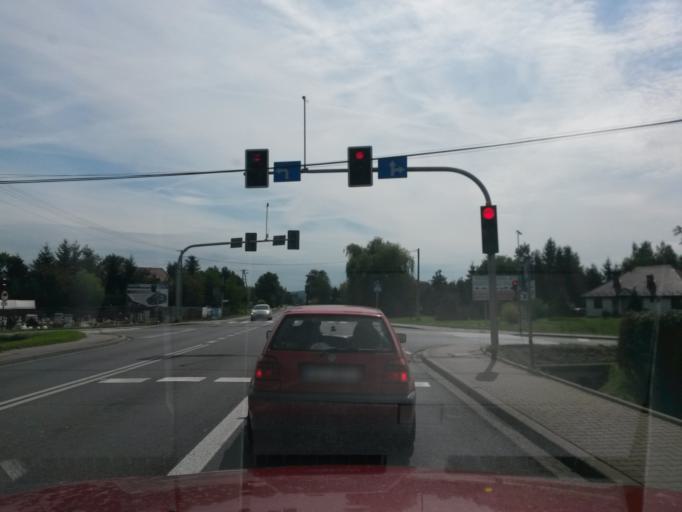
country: PL
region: Lesser Poland Voivodeship
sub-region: Powiat wielicki
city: Targowisko
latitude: 49.9818
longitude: 20.2882
